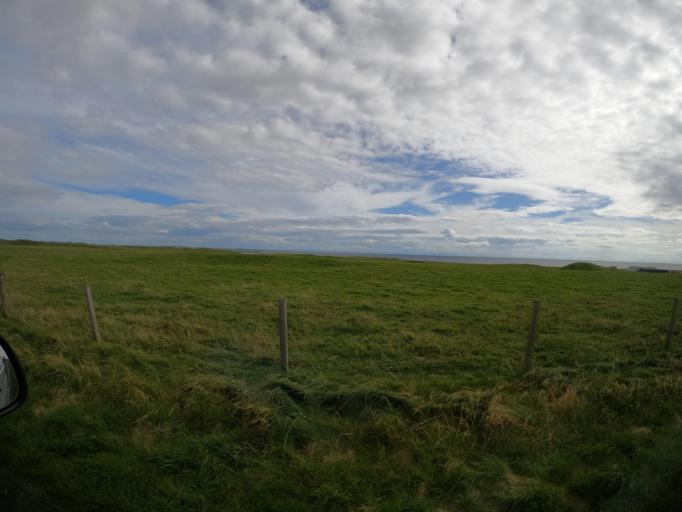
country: GB
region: Scotland
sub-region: Eilean Siar
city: Barra
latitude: 56.4756
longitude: -6.8995
